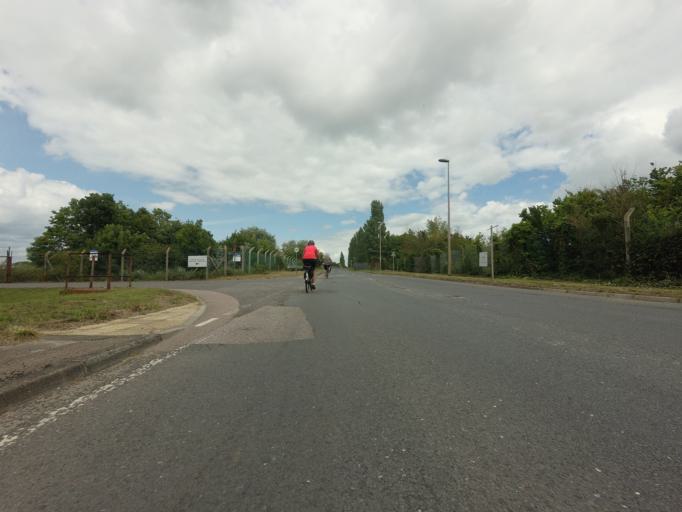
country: GB
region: England
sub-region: Medway
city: Allhallows
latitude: 51.4474
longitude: 0.6945
